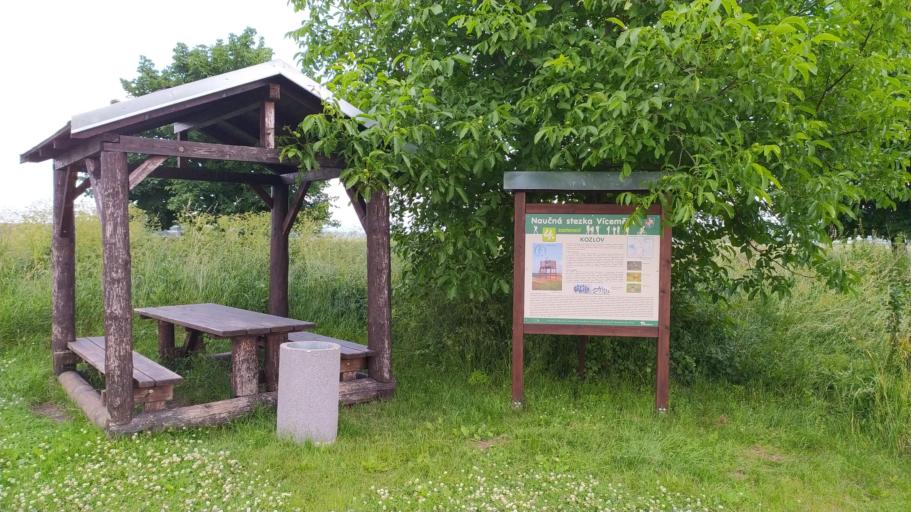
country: CZ
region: Olomoucky
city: Nezamyslice
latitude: 49.3472
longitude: 17.1823
